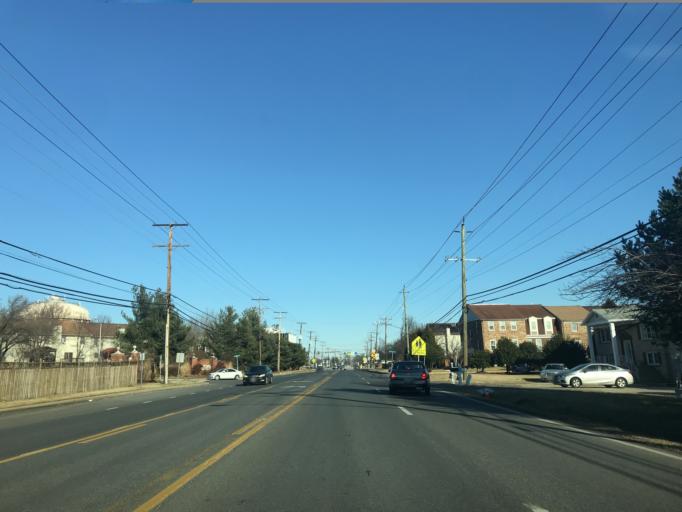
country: US
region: Maryland
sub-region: Prince George's County
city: Clinton
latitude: 38.7639
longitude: -76.9061
